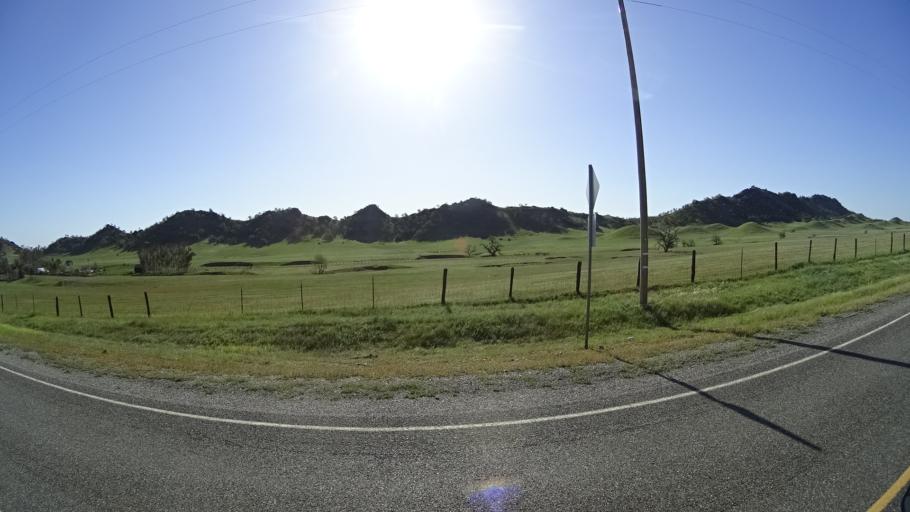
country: US
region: California
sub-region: Tehama County
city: Rancho Tehama Reserve
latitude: 39.7442
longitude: -122.5430
